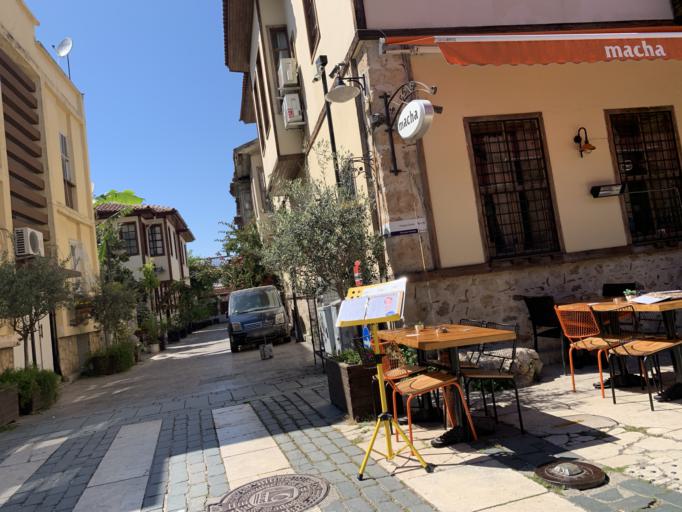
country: TR
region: Antalya
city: Antalya
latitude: 36.8823
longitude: 30.7053
